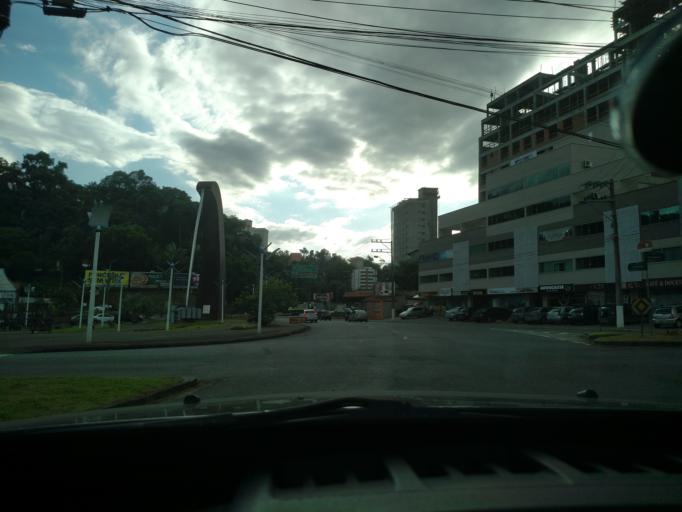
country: BR
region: Santa Catarina
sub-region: Blumenau
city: Blumenau
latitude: -26.8895
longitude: -49.0871
